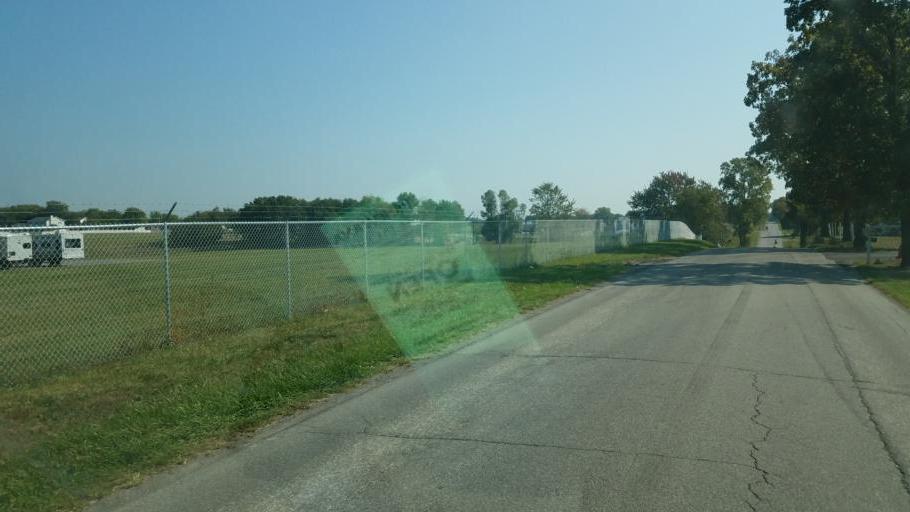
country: US
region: Indiana
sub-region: LaGrange County
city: Topeka
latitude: 41.6692
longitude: -85.5721
